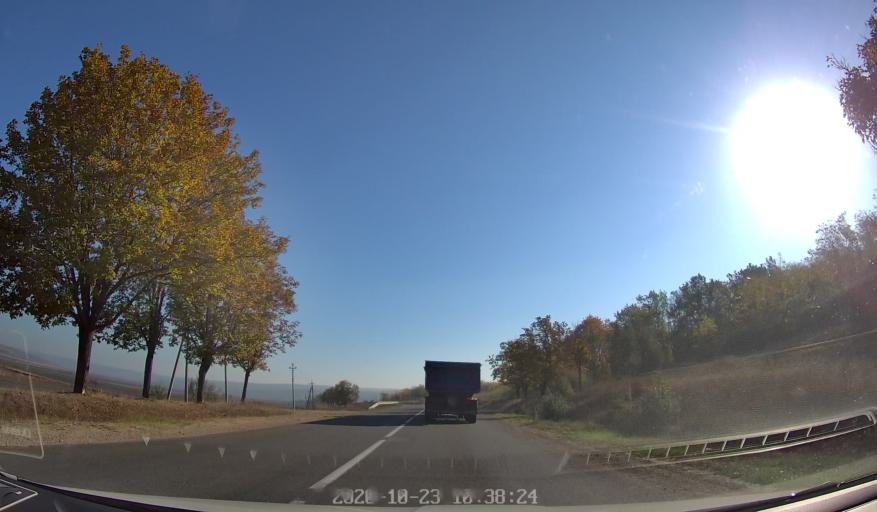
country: MD
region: Causeni
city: Causeni
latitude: 46.6669
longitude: 29.4696
